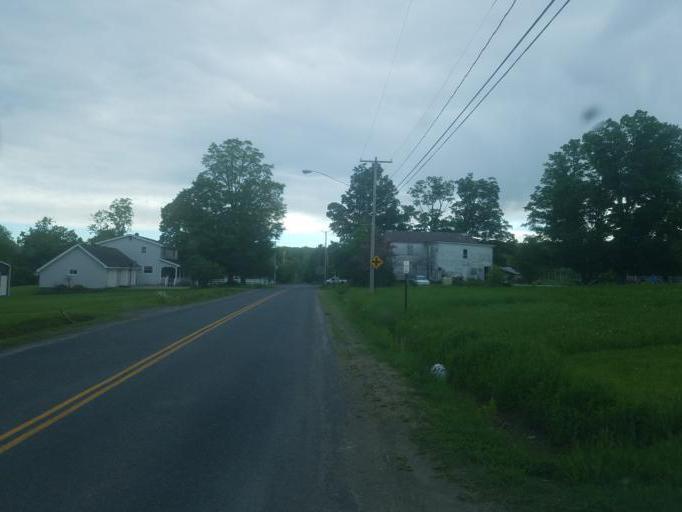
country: US
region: New York
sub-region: Herkimer County
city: Herkimer
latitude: 43.2074
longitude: -74.9524
